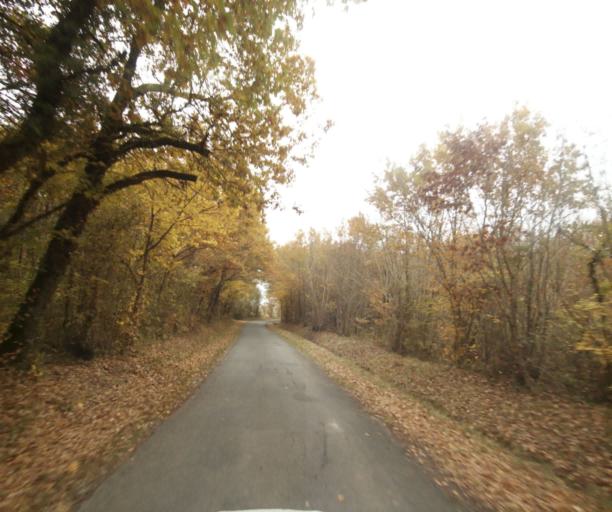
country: FR
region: Poitou-Charentes
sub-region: Departement de la Charente-Maritime
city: Chermignac
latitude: 45.7087
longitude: -0.6701
